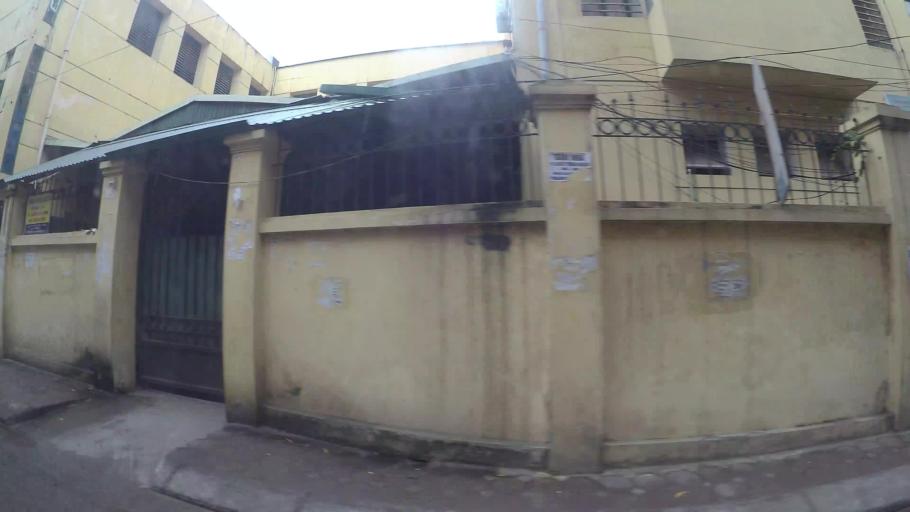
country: VN
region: Ha Noi
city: Dong Da
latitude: 21.0102
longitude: 105.8258
